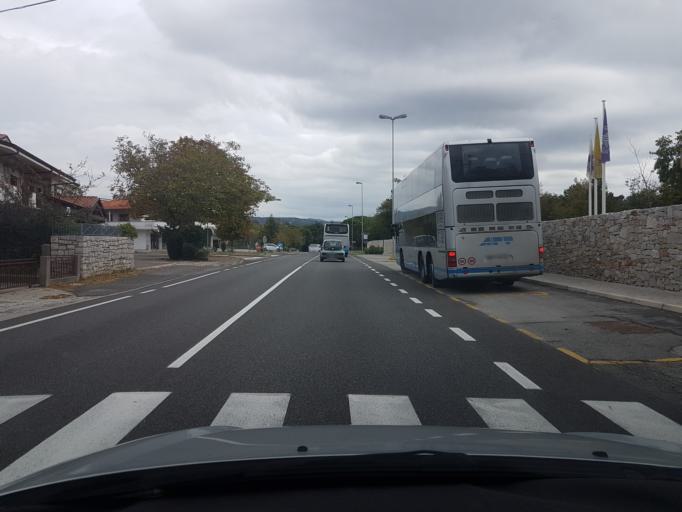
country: IT
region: Friuli Venezia Giulia
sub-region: Provincia di Trieste
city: Sistiana-Visogliano
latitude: 45.7730
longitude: 13.6243
